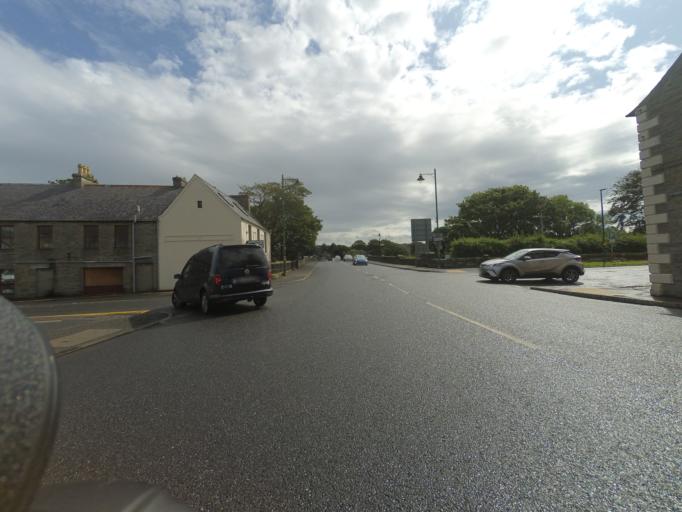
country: GB
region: Scotland
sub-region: Highland
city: Thurso
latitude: 58.5930
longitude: -3.5206
